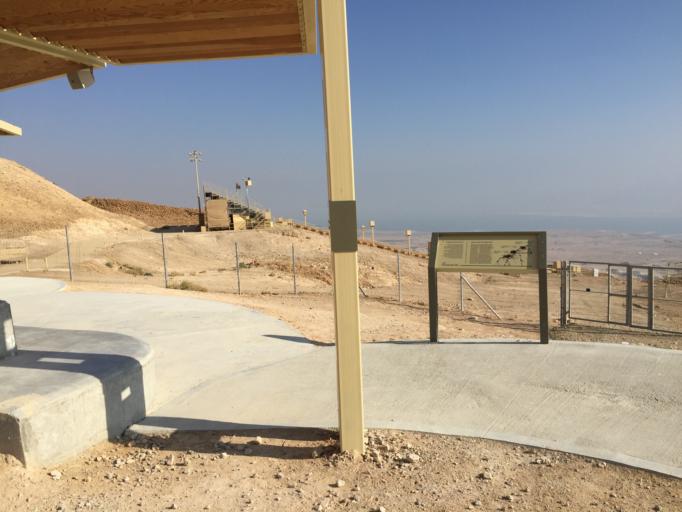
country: IL
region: Southern District
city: `En Boqeq
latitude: 31.3185
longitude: 35.3482
